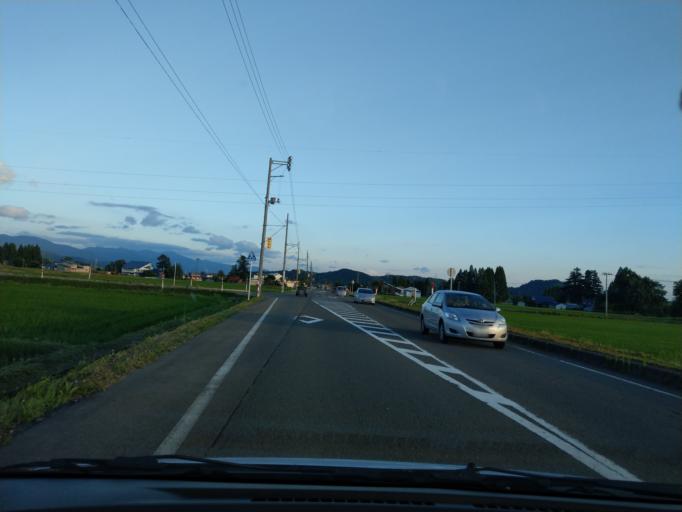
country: JP
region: Akita
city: Kakunodatemachi
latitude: 39.6293
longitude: 140.5707
